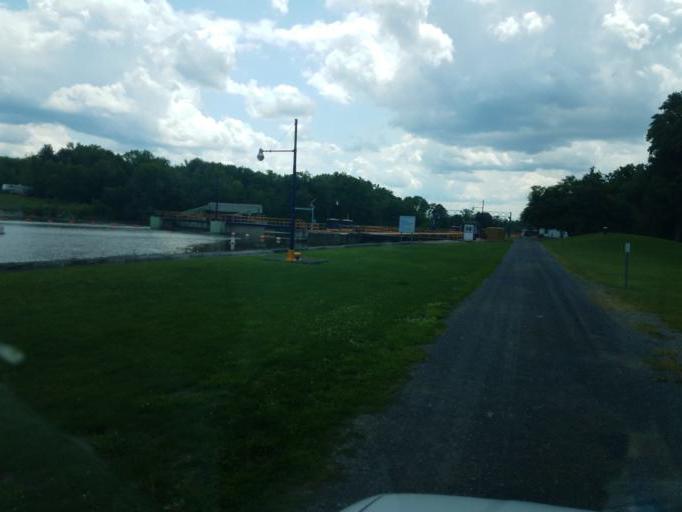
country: US
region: New York
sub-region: Wayne County
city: Clyde
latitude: 43.0601
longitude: -76.8390
